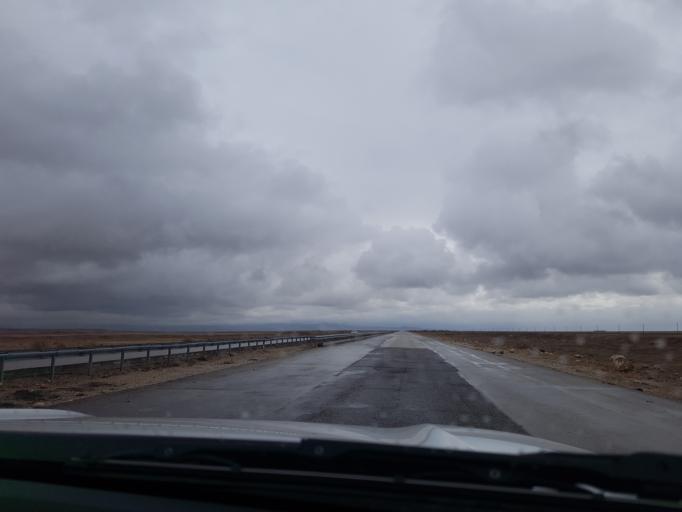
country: TM
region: Balkan
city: Balkanabat
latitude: 39.8782
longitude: 54.0592
